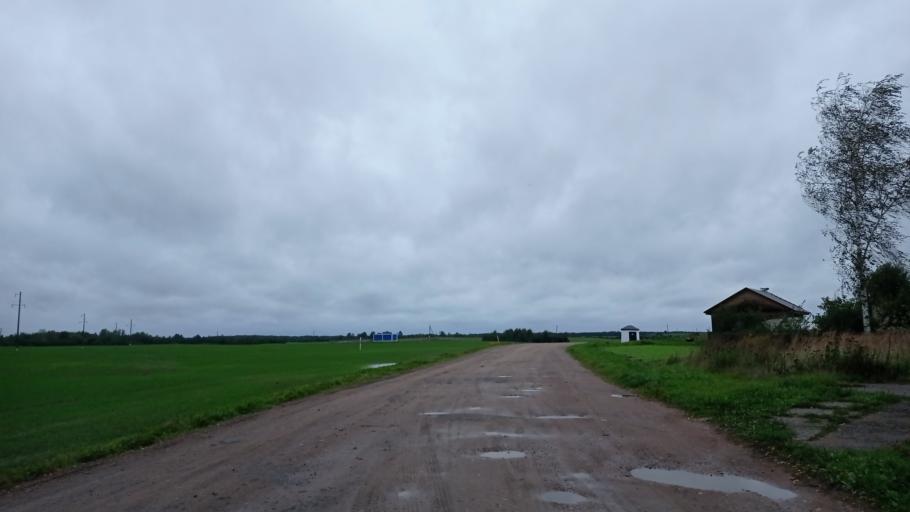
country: BY
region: Vitebsk
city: Haradok
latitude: 55.3385
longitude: 30.0946
